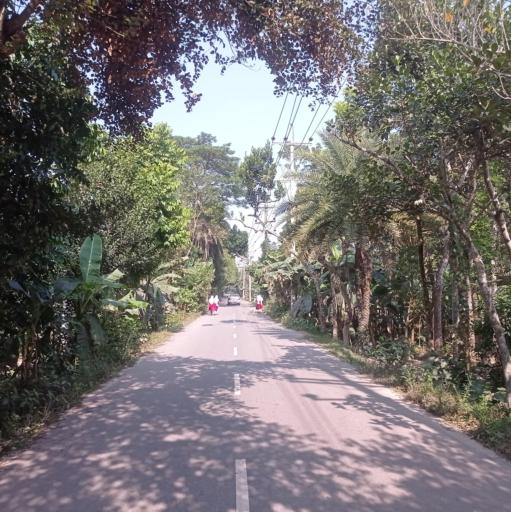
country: BD
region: Dhaka
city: Narsingdi
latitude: 24.0722
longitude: 90.6928
